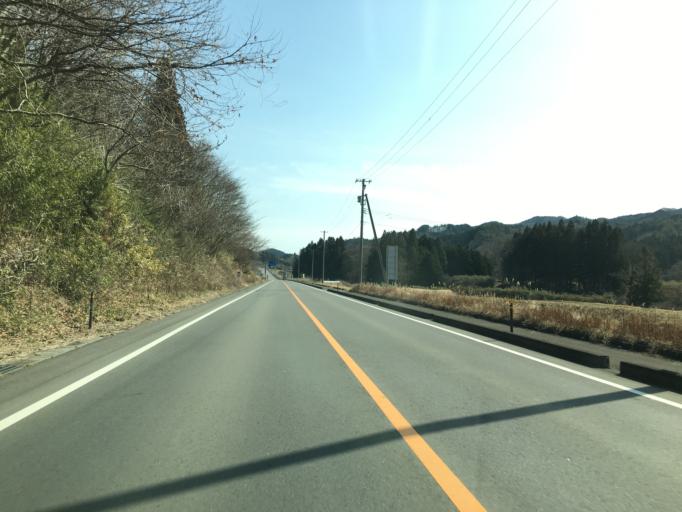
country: JP
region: Ibaraki
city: Daigo
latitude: 36.8188
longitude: 140.4606
